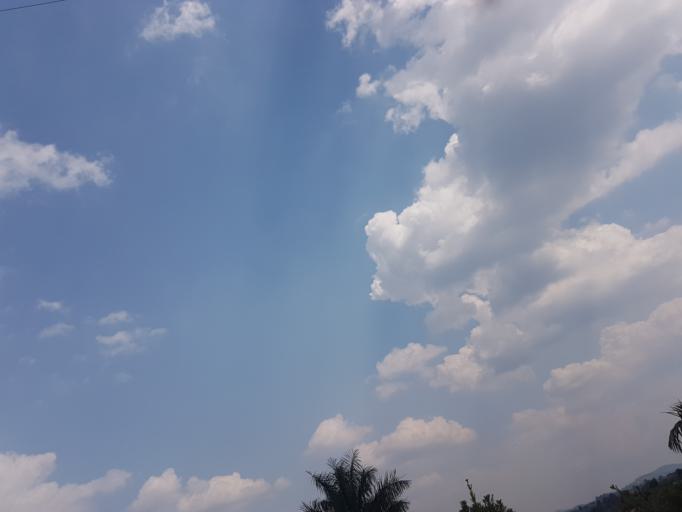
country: UG
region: Western Region
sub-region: Bushenyi District
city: Bushenyi
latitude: -0.5415
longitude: 30.1310
